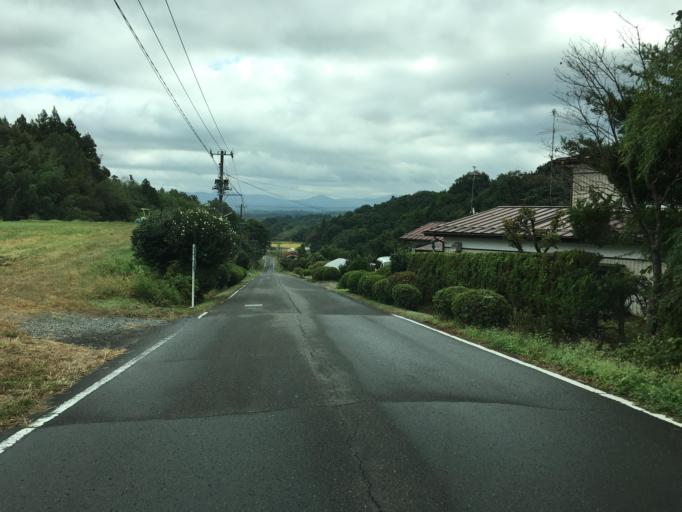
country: JP
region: Fukushima
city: Nihommatsu
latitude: 37.6293
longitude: 140.4381
